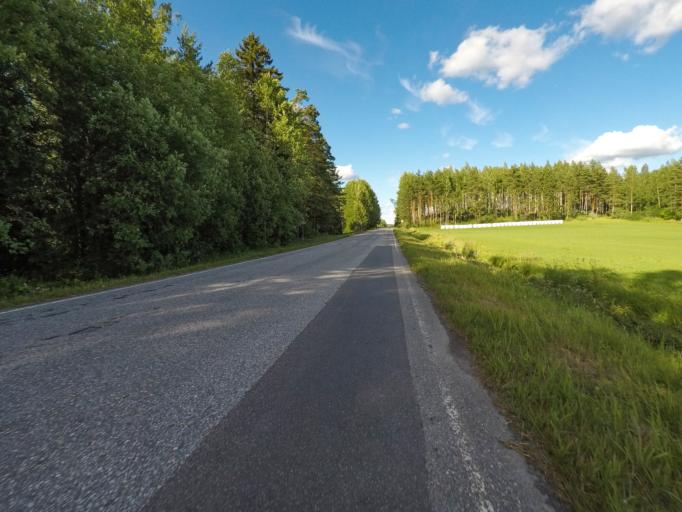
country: FI
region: South Karelia
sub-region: Imatra
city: Imatra
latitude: 61.1317
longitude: 28.7258
